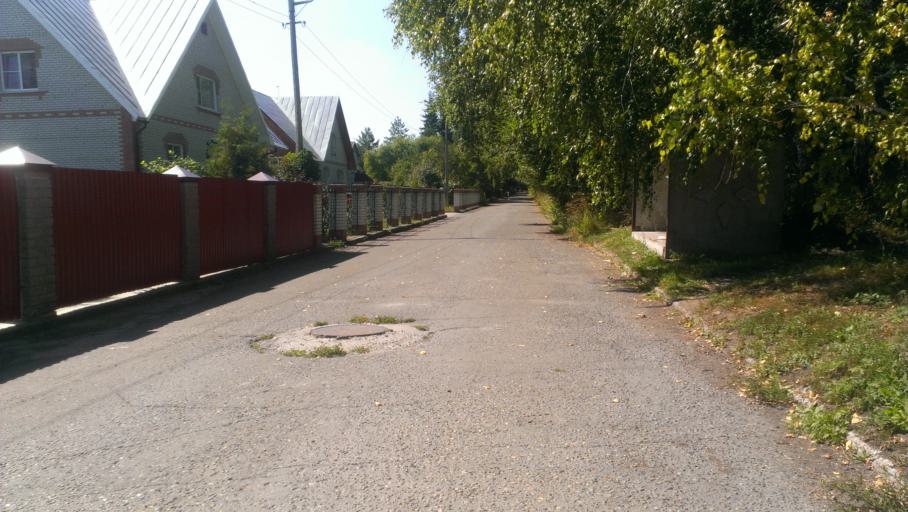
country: RU
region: Altai Krai
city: Nauchnyy Gorodok
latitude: 53.4222
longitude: 83.5158
